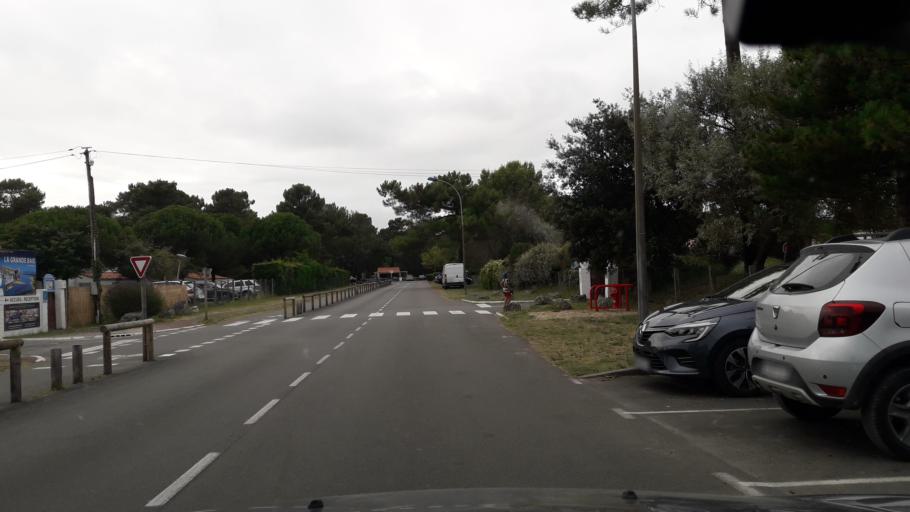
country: FR
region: Poitou-Charentes
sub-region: Departement de la Charente-Maritime
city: Les Mathes
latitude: 45.6900
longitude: -1.1875
